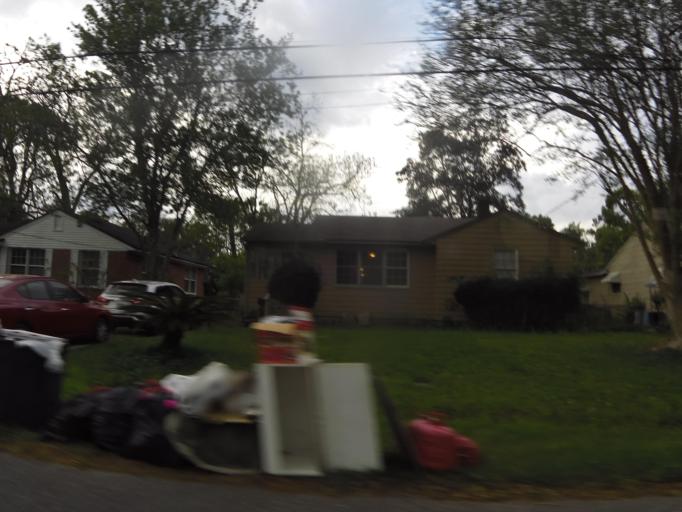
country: US
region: Florida
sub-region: Duval County
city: Jacksonville
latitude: 30.2868
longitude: -81.7270
